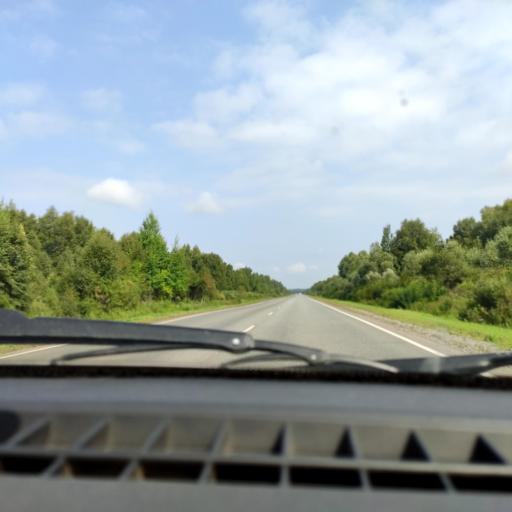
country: RU
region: Bashkortostan
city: Mikhaylovka
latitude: 54.9000
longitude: 55.7260
